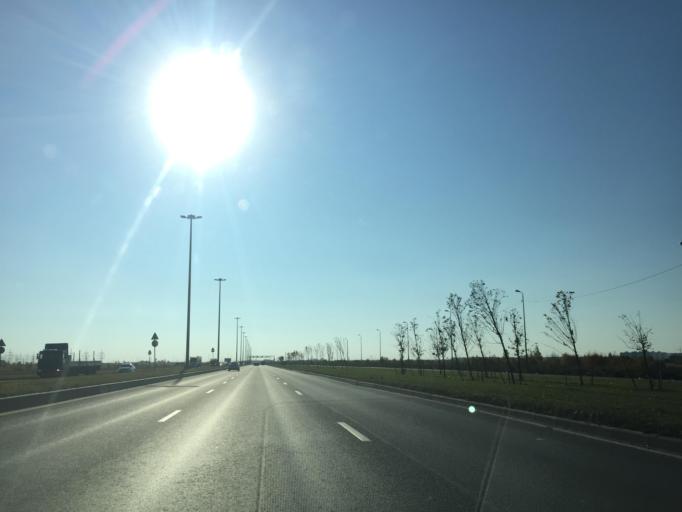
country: RU
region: St.-Petersburg
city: Petro-Slavyanka
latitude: 59.7768
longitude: 30.4984
